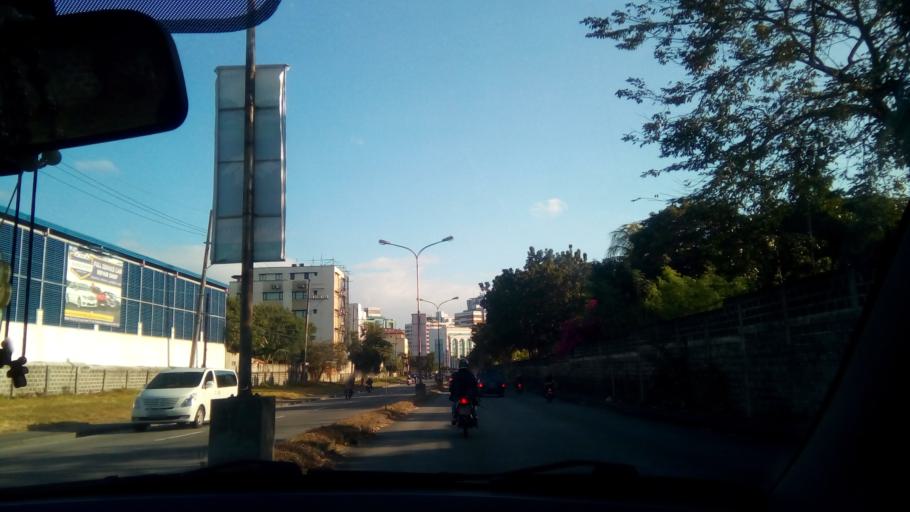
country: PH
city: Sambayanihan People's Village
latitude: 14.4142
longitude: 121.0168
